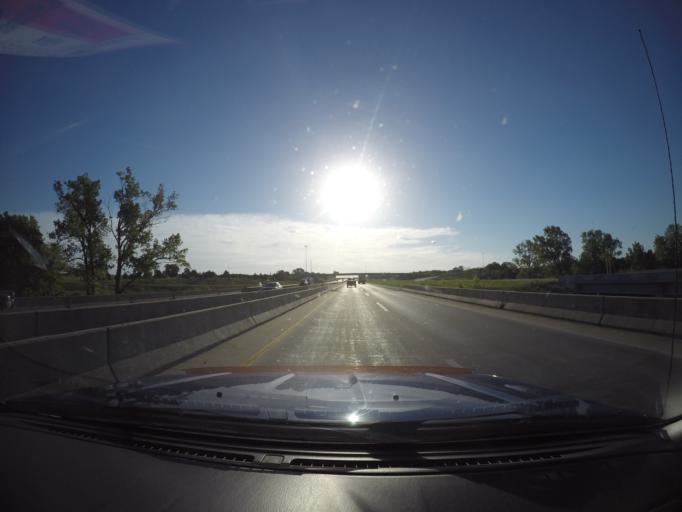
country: US
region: Kansas
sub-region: Wyandotte County
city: Bonner Springs
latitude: 39.0951
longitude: -94.8914
